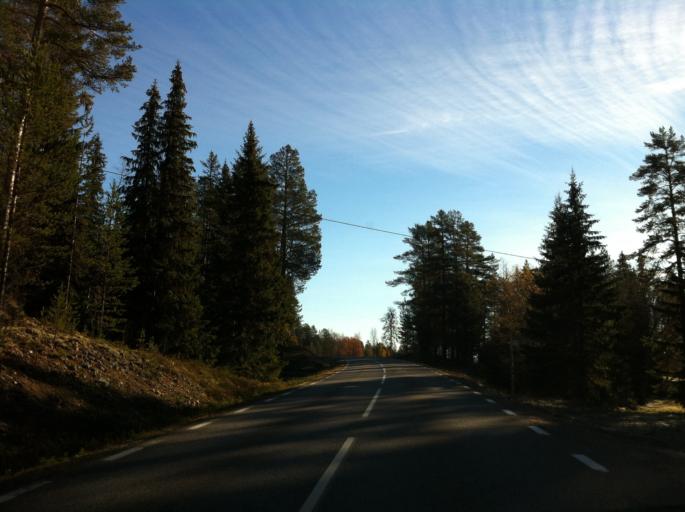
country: NO
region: Hedmark
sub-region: Engerdal
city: Engerdal
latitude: 62.0006
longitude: 12.4485
